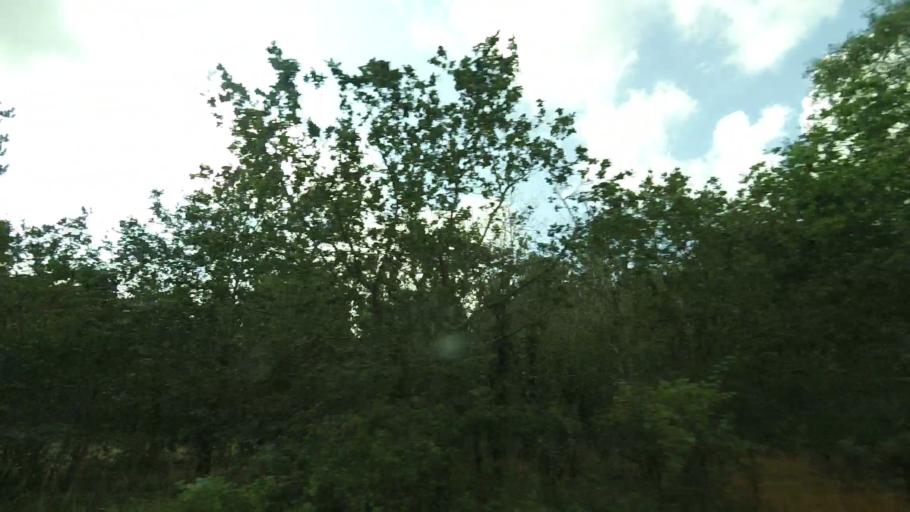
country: DK
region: Central Jutland
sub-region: Norddjurs Kommune
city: Auning
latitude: 56.5115
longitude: 10.4108
